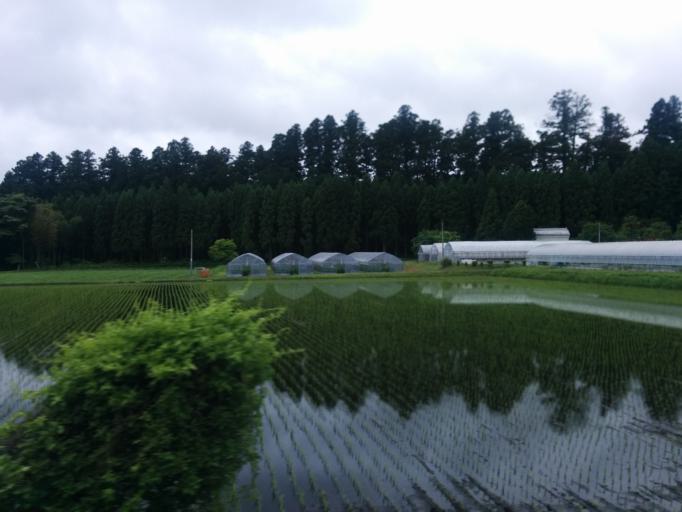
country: JP
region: Tochigi
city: Imaichi
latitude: 36.7099
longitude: 139.7021
